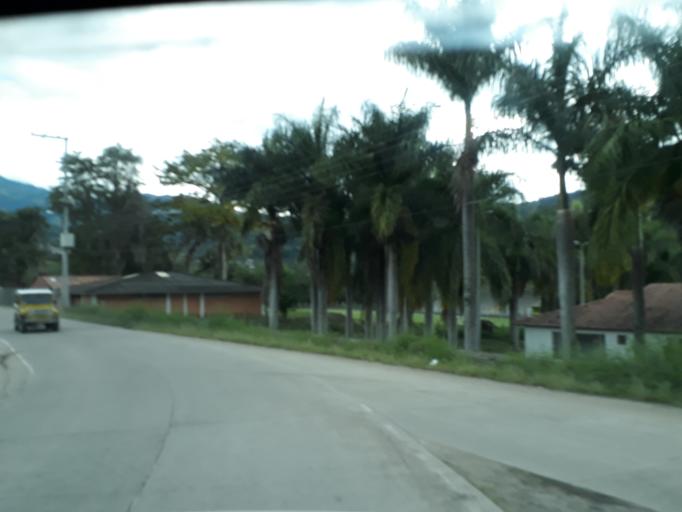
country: CO
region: Cundinamarca
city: Pacho
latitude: 5.1507
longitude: -74.1536
